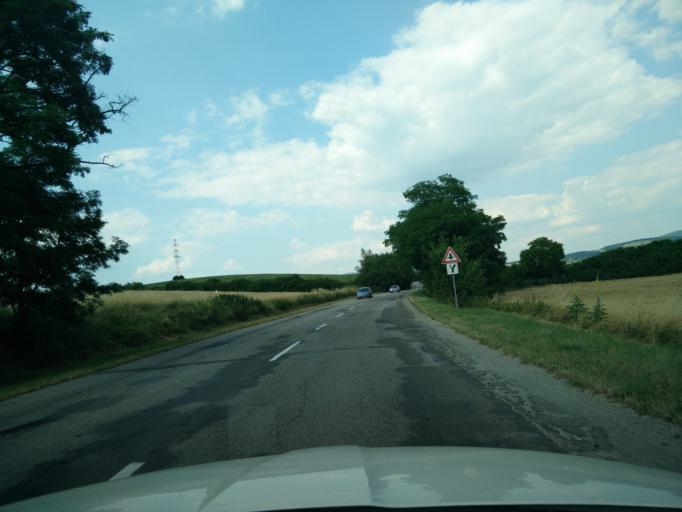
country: SK
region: Nitriansky
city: Partizanske
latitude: 48.6412
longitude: 18.3579
